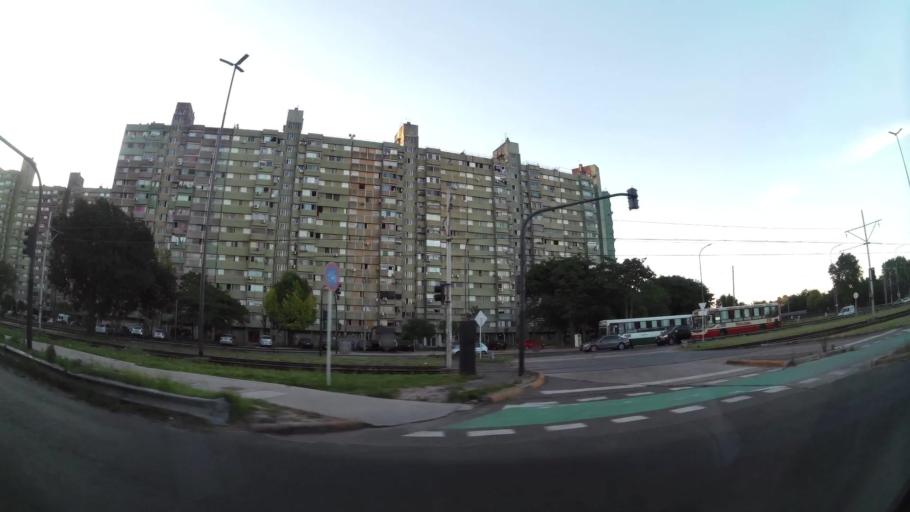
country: AR
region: Buenos Aires F.D.
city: Villa Lugano
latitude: -34.6873
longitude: -58.4581
